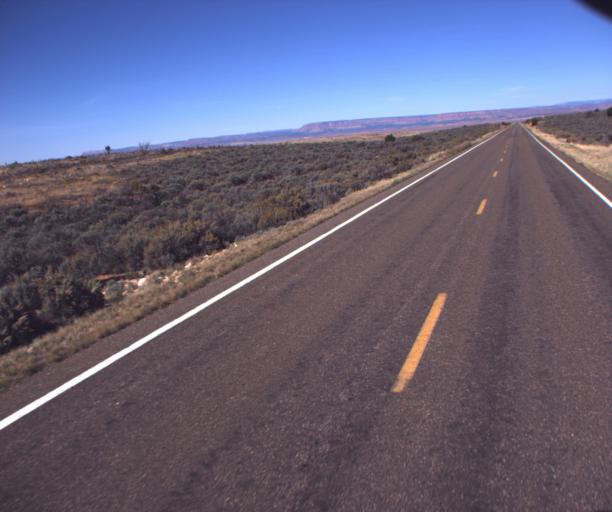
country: US
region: Arizona
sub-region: Coconino County
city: Fredonia
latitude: 36.8630
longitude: -112.3140
